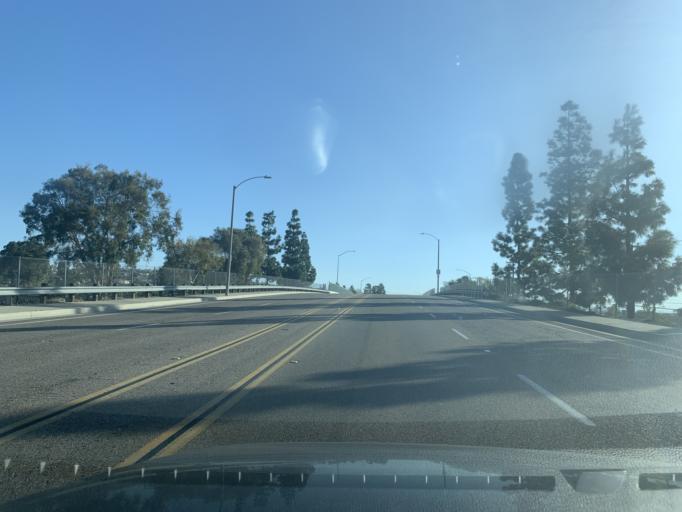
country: US
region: California
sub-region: Orange County
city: Villa Park
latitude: 33.8230
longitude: -117.8336
